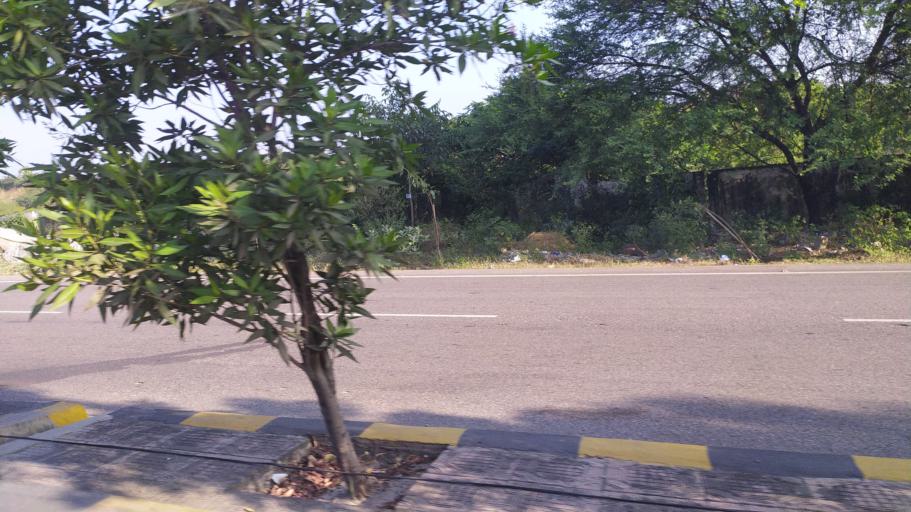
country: IN
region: Telangana
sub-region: Hyderabad
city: Hyderabad
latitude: 17.3204
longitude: 78.3876
